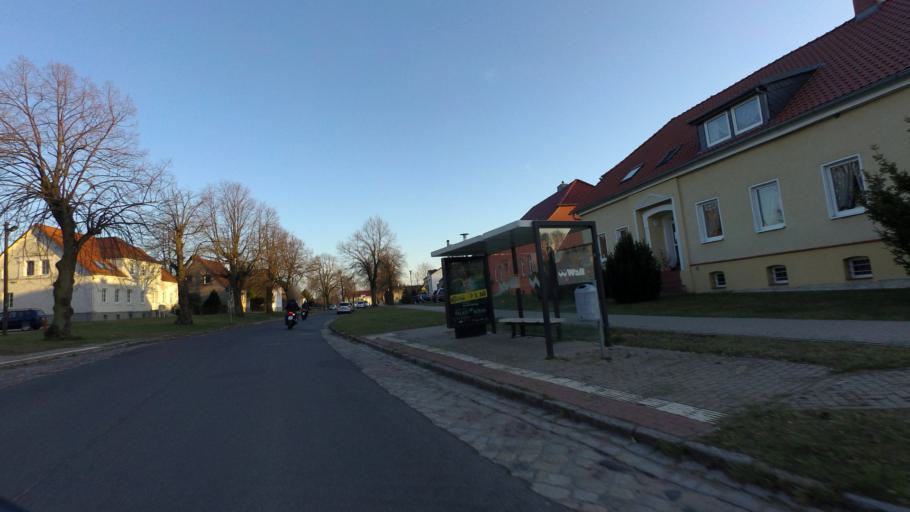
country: DE
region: Berlin
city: Hellersdorf
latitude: 52.5453
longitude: 13.6386
